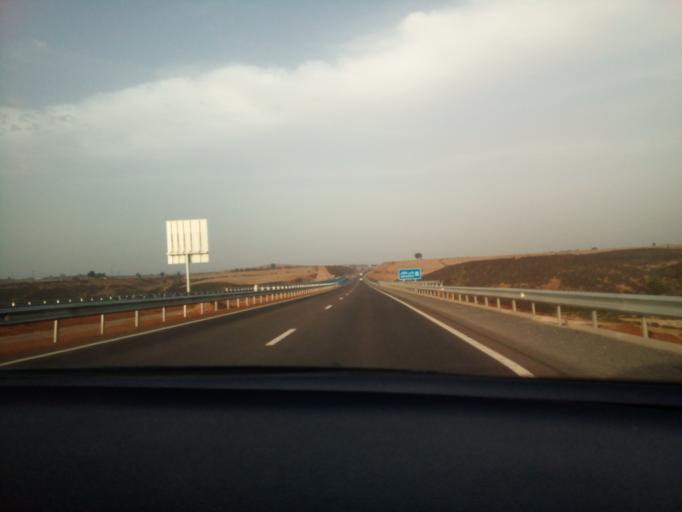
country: MA
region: Rabat-Sale-Zemmour-Zaer
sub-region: Skhirate-Temara
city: Temara
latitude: 33.8526
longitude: -6.8265
